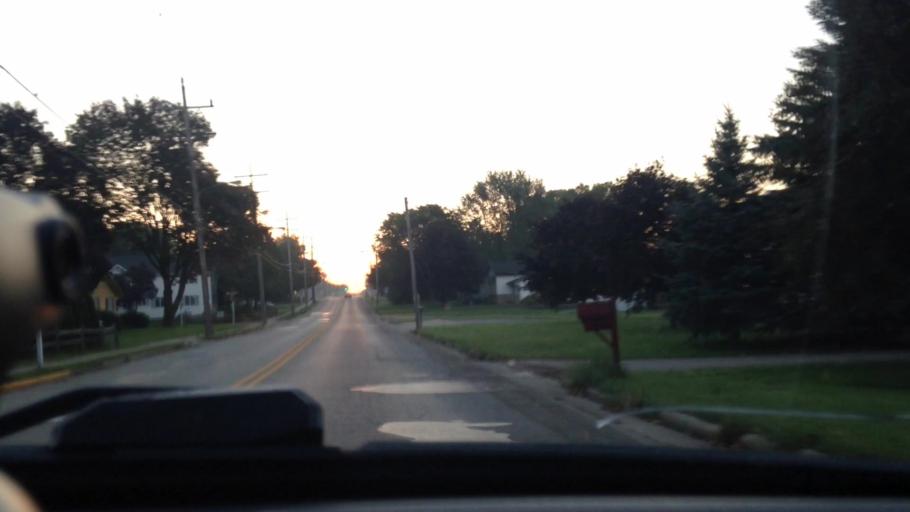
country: US
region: Wisconsin
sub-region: Dodge County
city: Lomira
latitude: 43.5871
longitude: -88.4384
